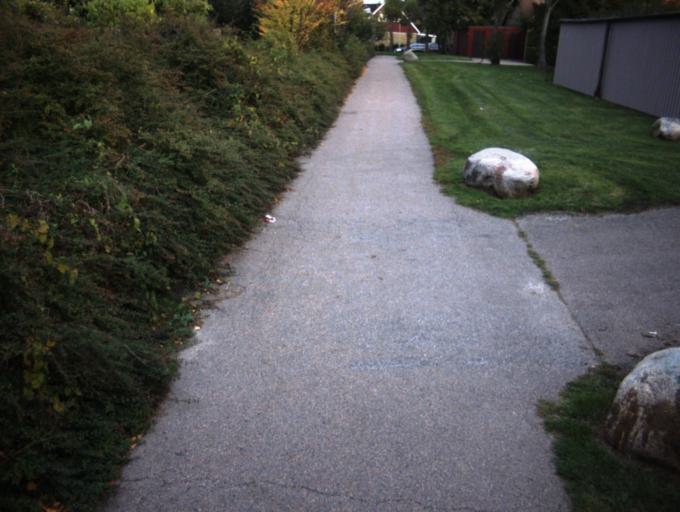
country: SE
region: Skane
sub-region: Helsingborg
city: Odakra
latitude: 56.1004
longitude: 12.7576
